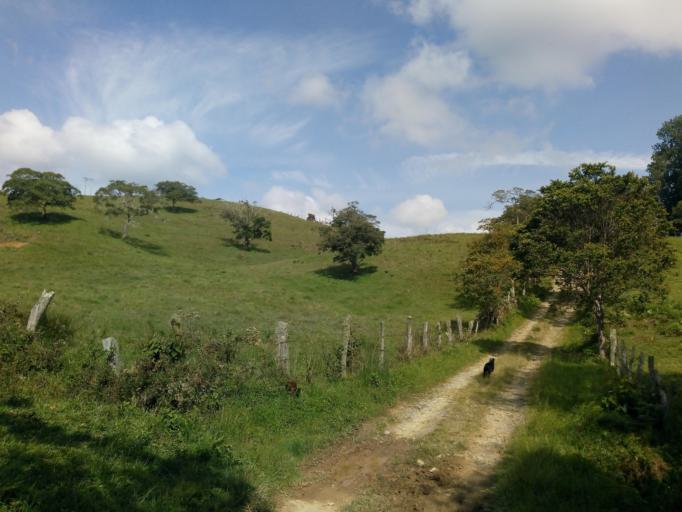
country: CO
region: Boyaca
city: Moniquira
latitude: 5.8668
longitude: -73.5014
